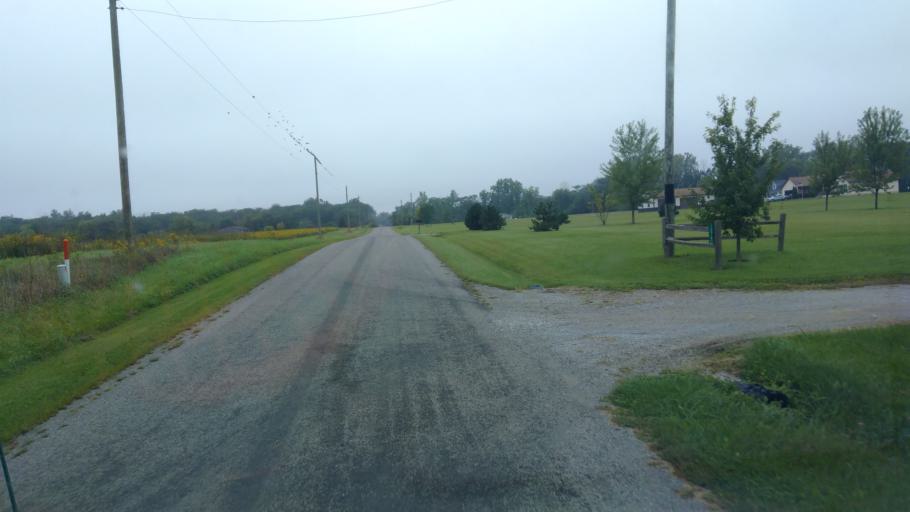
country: US
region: Ohio
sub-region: Union County
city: Richwood
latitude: 40.4825
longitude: -83.4267
